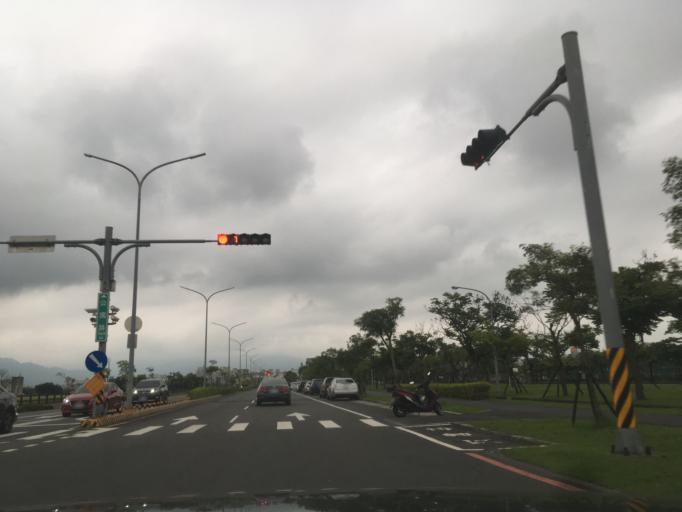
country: TW
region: Taiwan
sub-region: Yilan
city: Yilan
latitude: 24.7359
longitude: 121.7515
